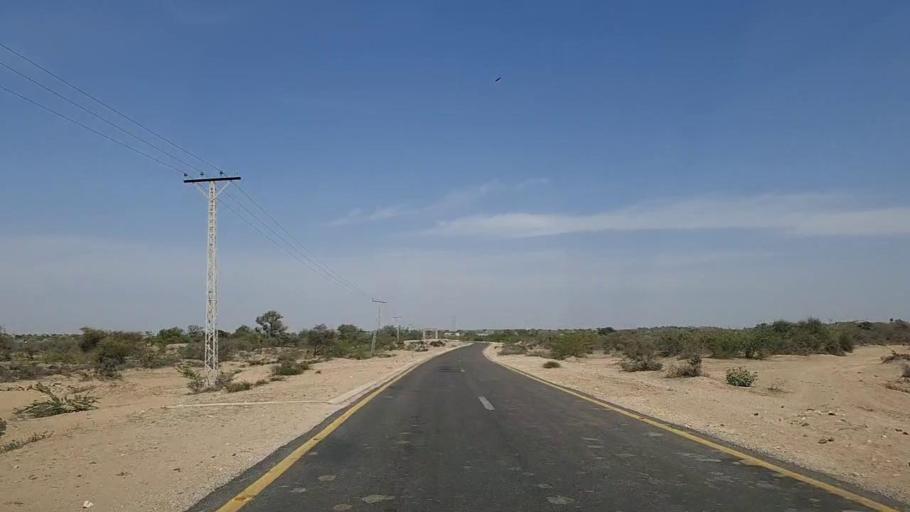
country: PK
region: Sindh
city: Mithi
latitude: 24.9640
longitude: 69.9106
